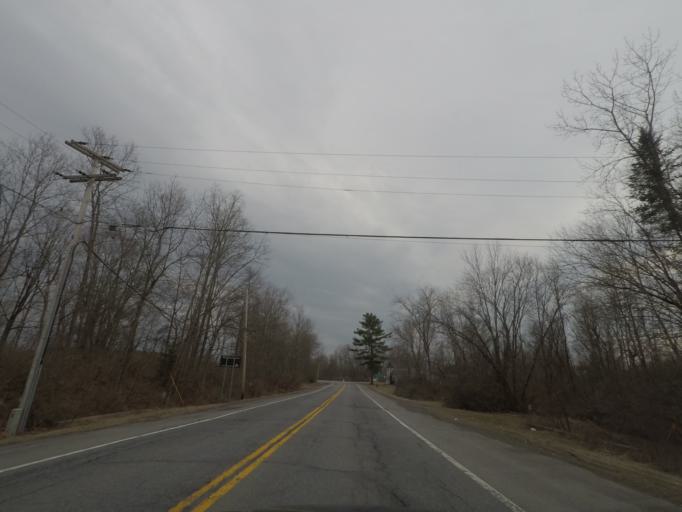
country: US
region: New York
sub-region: Saratoga County
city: Schuylerville
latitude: 43.1626
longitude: -73.5782
